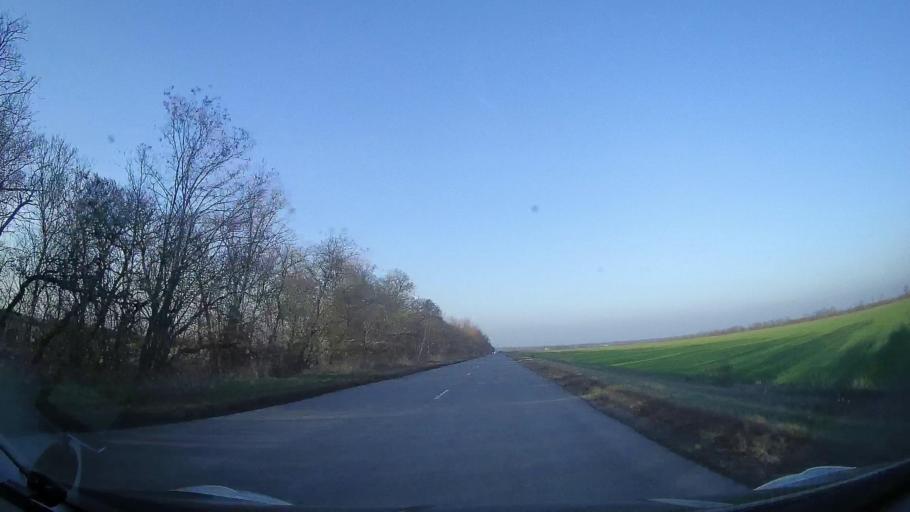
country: RU
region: Rostov
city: Kirovskaya
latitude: 47.0113
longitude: 39.9790
